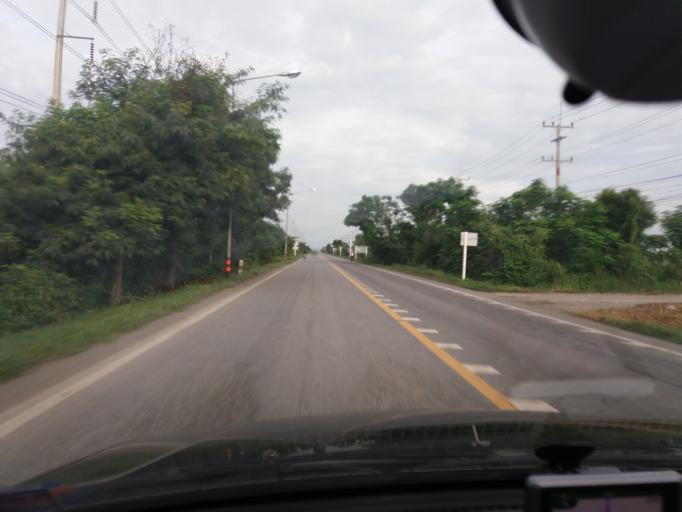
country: TH
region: Suphan Buri
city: U Thong
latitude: 14.3358
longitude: 99.8020
